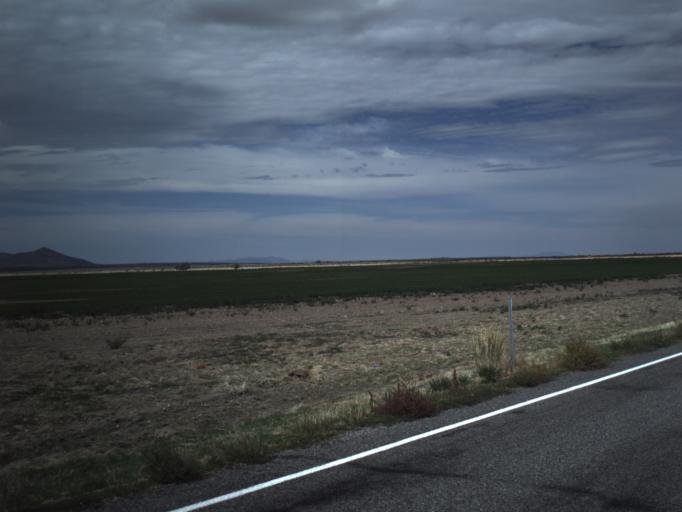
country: US
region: Utah
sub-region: Millard County
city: Fillmore
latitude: 39.0544
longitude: -112.4098
